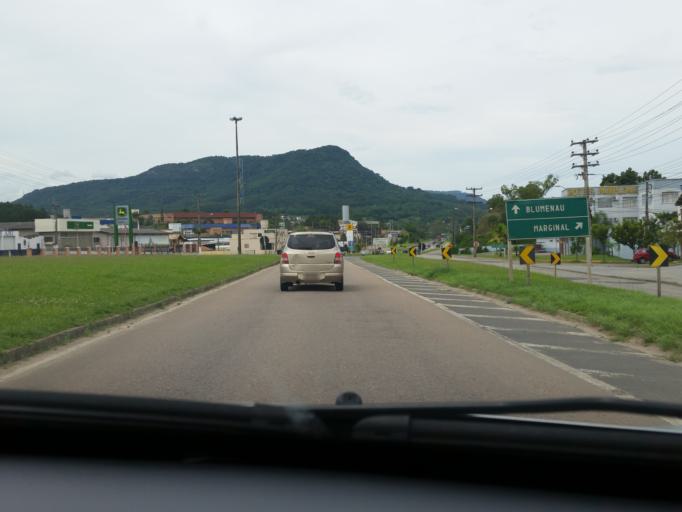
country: BR
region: Santa Catarina
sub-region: Rio Do Sul
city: Rio do Sul
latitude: -27.1995
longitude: -49.6304
